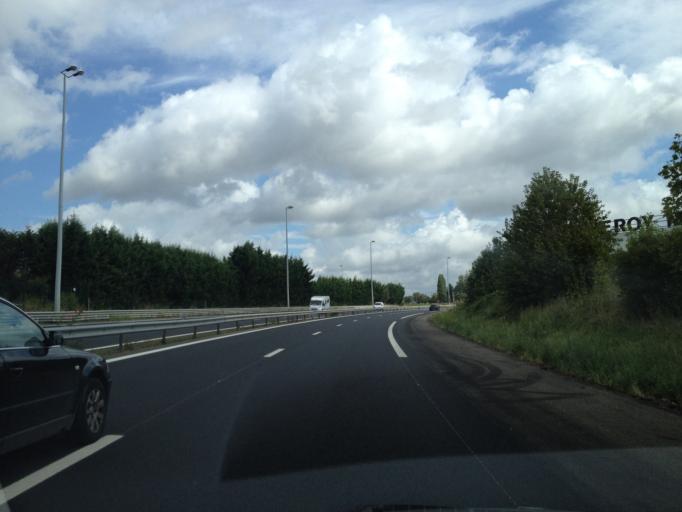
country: FR
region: Haute-Normandie
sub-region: Departement de la Seine-Maritime
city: Isneauville
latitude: 49.4873
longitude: 1.1407
